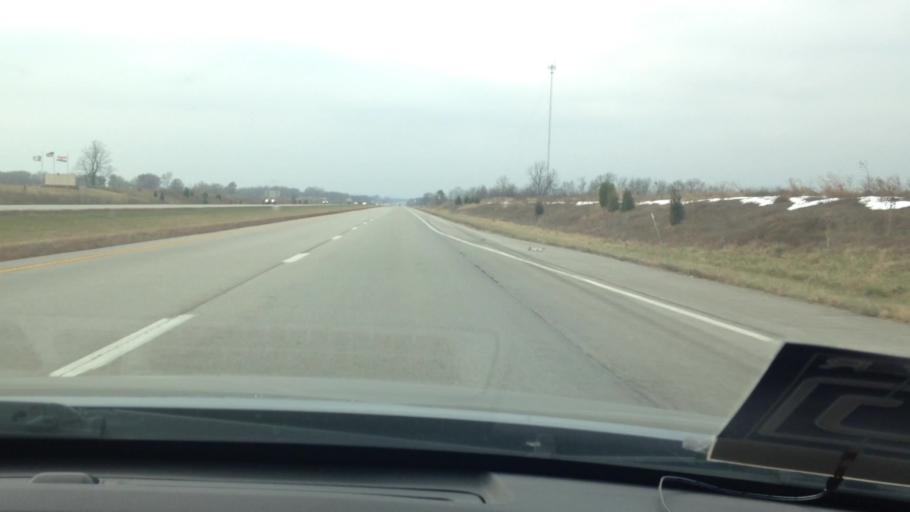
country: US
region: Missouri
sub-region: Cass County
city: Garden City
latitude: 38.5749
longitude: -94.1993
